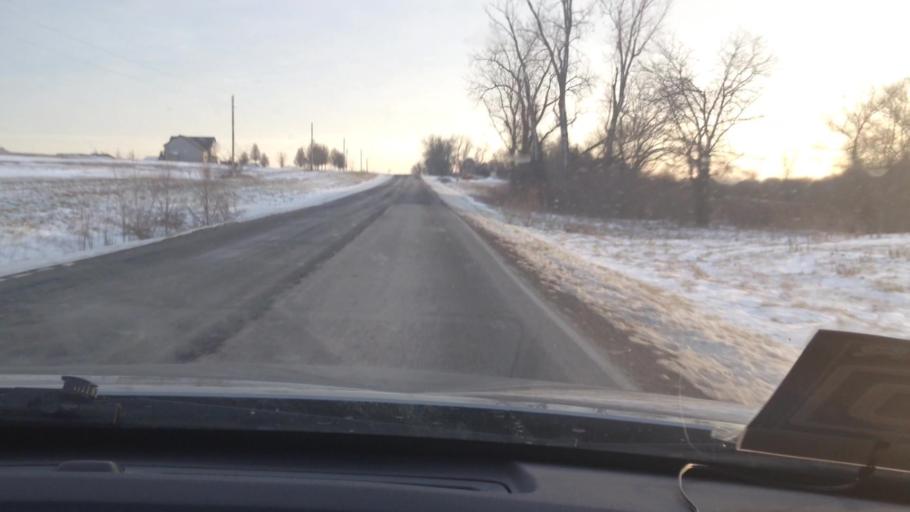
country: US
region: Kansas
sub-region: Leavenworth County
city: Lansing
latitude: 39.2360
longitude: -94.9751
